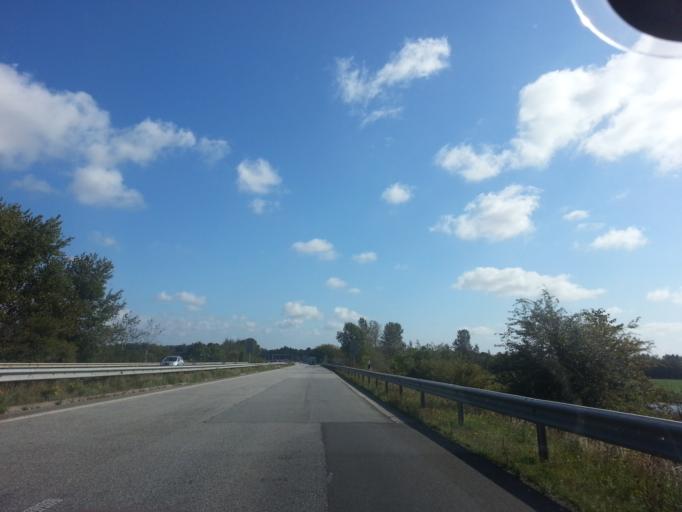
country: DE
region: Schleswig-Holstein
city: Neustadt in Holstein
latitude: 54.1247
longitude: 10.8111
